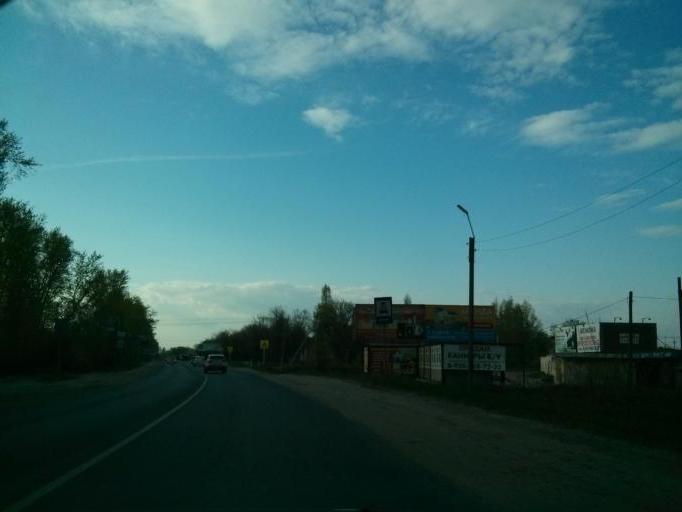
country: RU
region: Vladimir
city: Murom
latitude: 55.5971
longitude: 42.0336
